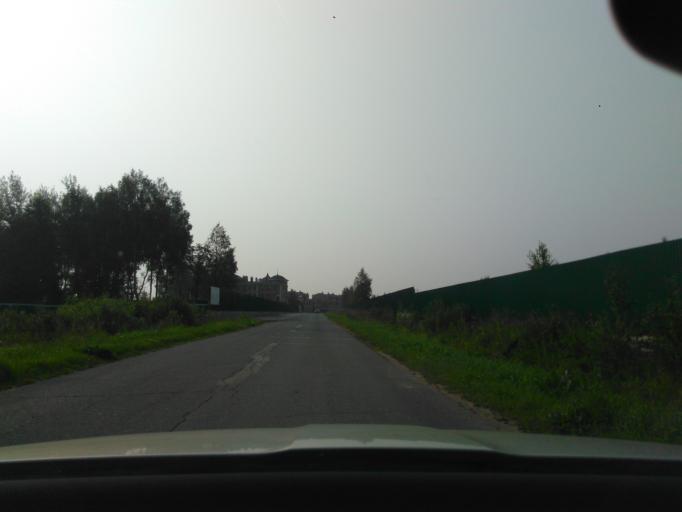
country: RU
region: Tverskaya
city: Konakovo
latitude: 56.6785
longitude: 36.7085
